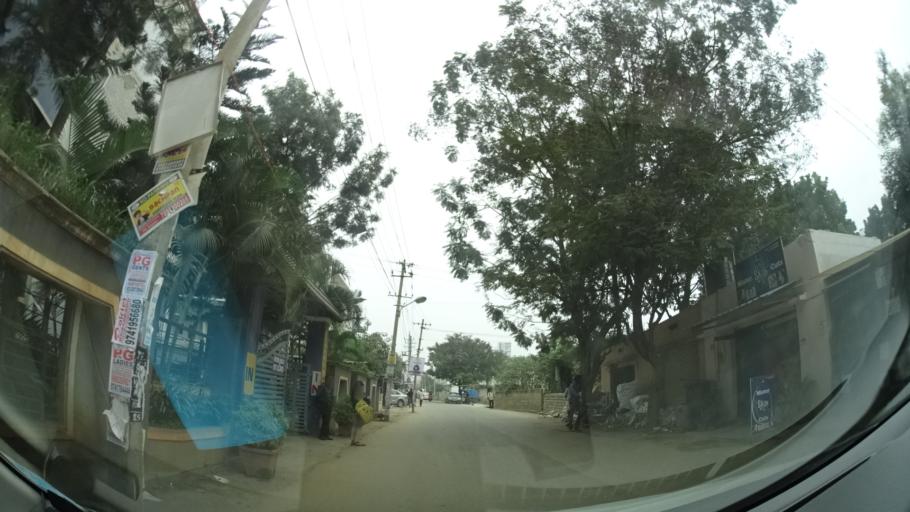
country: IN
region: Karnataka
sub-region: Bangalore Rural
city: Hoskote
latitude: 12.9829
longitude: 77.7472
